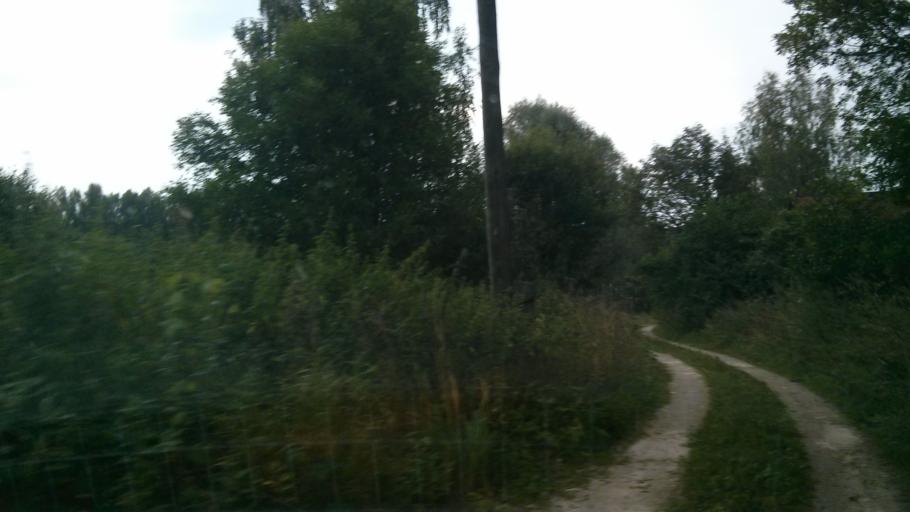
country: RU
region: Nizjnij Novgorod
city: Shimorskoye
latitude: 55.3074
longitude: 41.8499
